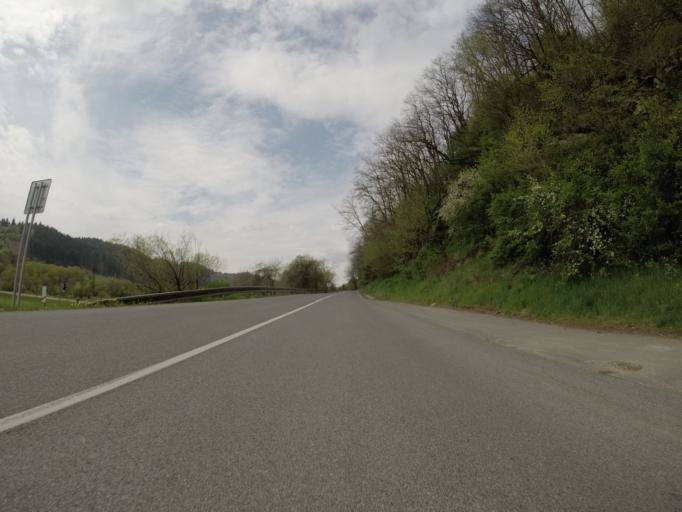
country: SK
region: Banskobystricky
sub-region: Okres Banska Bystrica
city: Brezno
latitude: 48.8246
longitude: 19.7293
